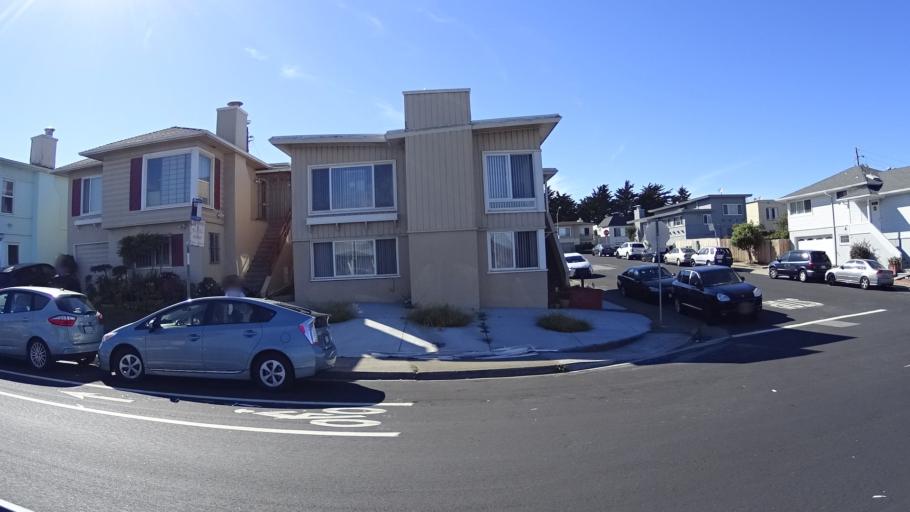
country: US
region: California
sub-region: San Mateo County
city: Broadmoor
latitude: 37.6858
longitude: -122.4872
